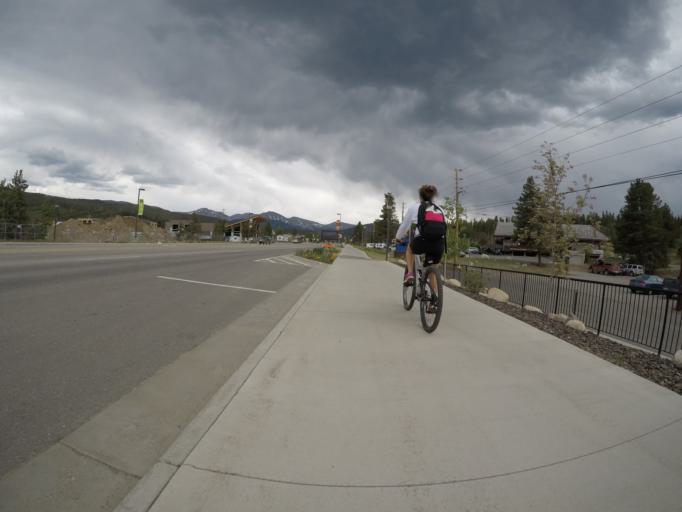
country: US
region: Colorado
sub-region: Grand County
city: Fraser
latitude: 39.9266
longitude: -105.7883
